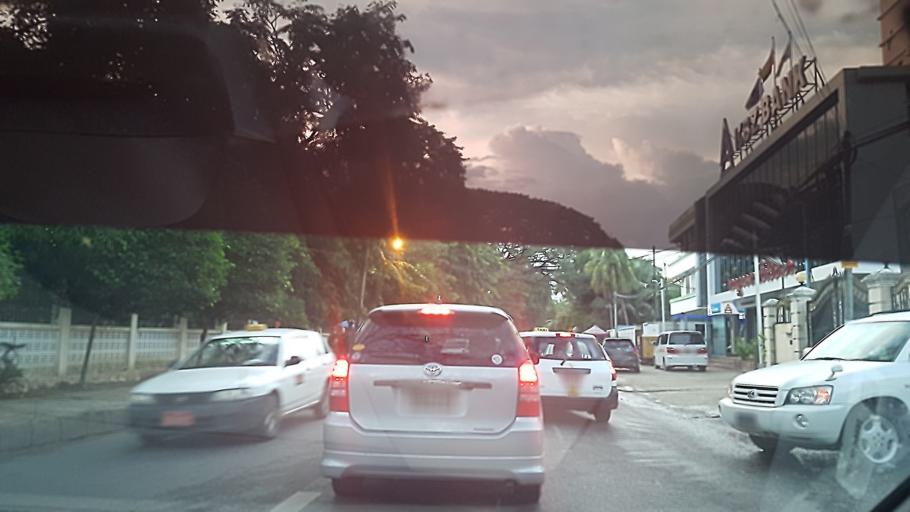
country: MM
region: Yangon
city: Yangon
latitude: 16.8095
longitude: 96.1432
